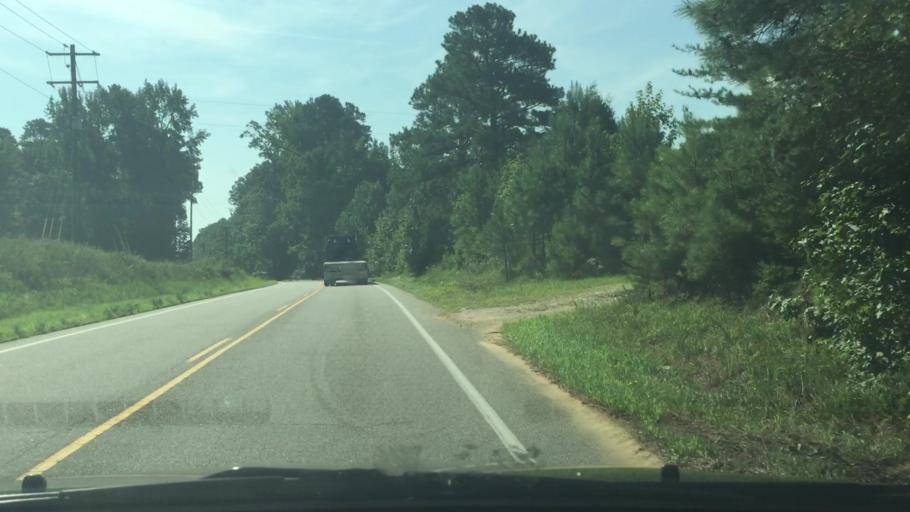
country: US
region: Virginia
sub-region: Sussex County
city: Sussex
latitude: 37.0567
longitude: -77.3264
